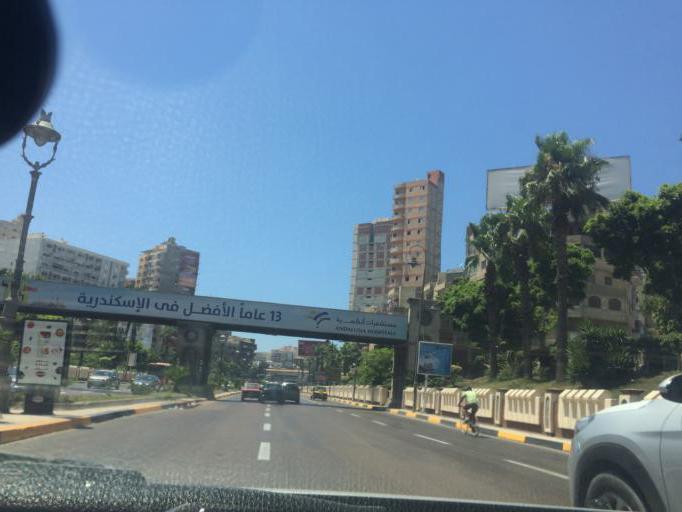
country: EG
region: Alexandria
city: Alexandria
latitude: 31.1955
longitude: 29.9203
